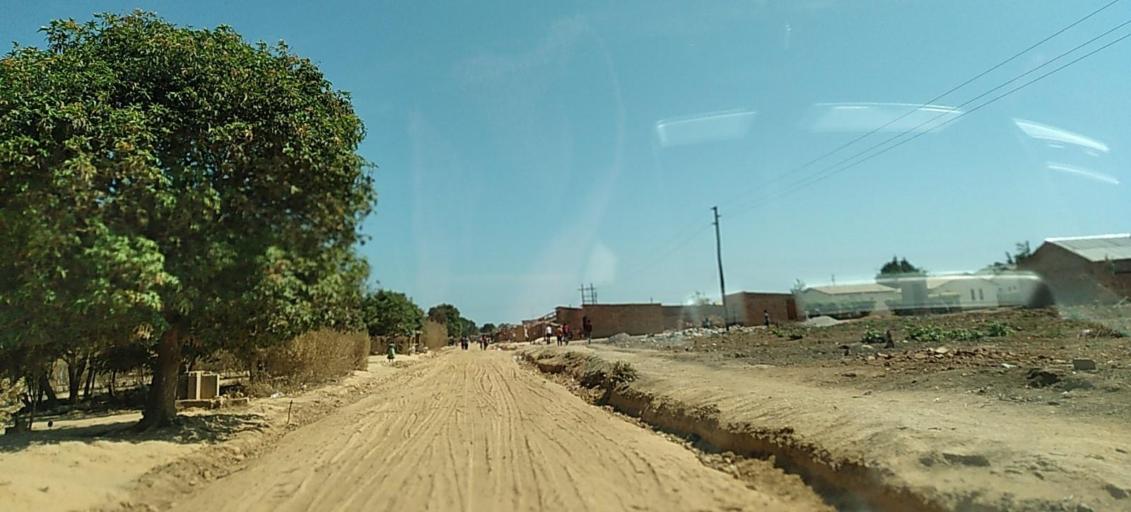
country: ZM
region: Copperbelt
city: Chililabombwe
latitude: -12.3291
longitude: 27.8603
